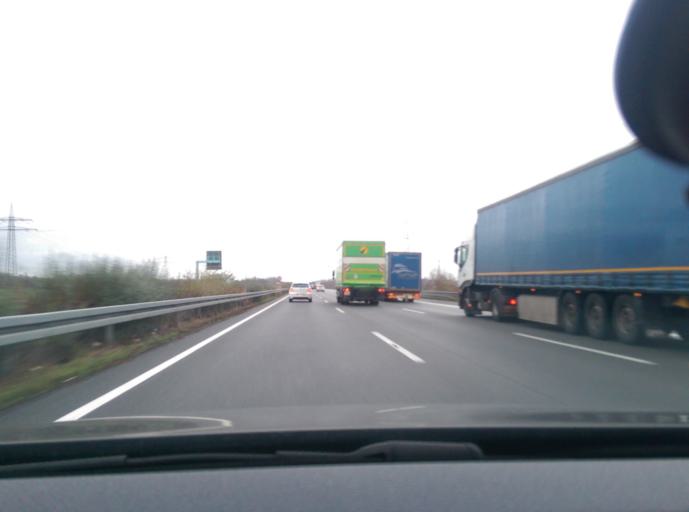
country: DE
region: Lower Saxony
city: Rosdorf
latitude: 51.5057
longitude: 9.8783
